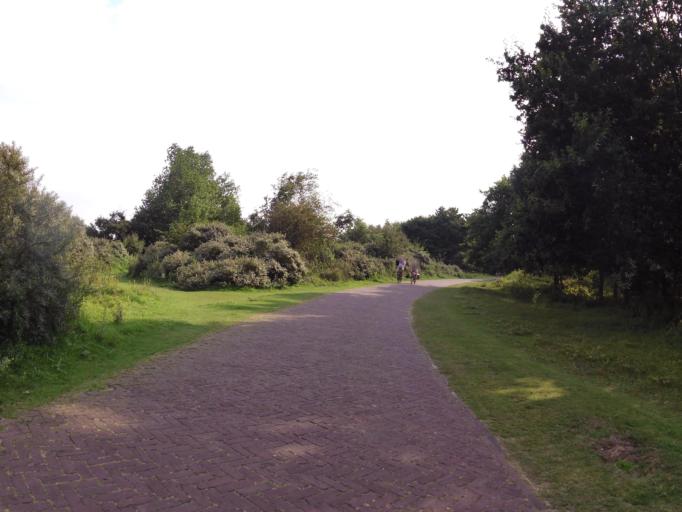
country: NL
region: North Holland
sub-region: Gemeente Bergen
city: Egmond aan Zee
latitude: 52.6011
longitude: 4.6409
